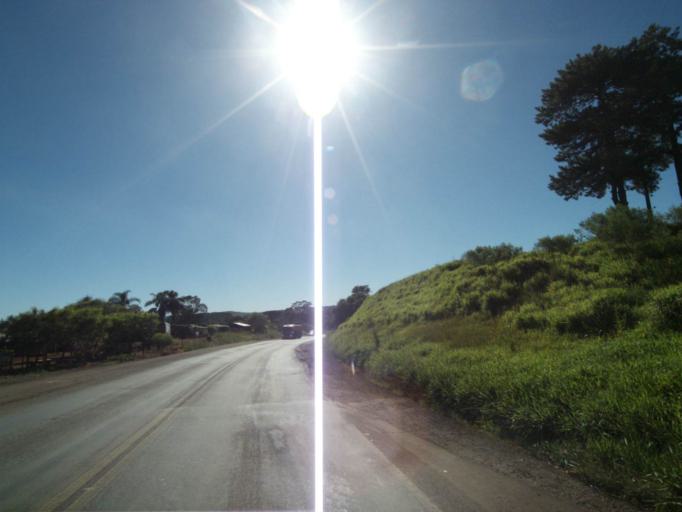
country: BR
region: Parana
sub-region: Pato Branco
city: Pato Branco
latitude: -26.2559
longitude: -52.7829
